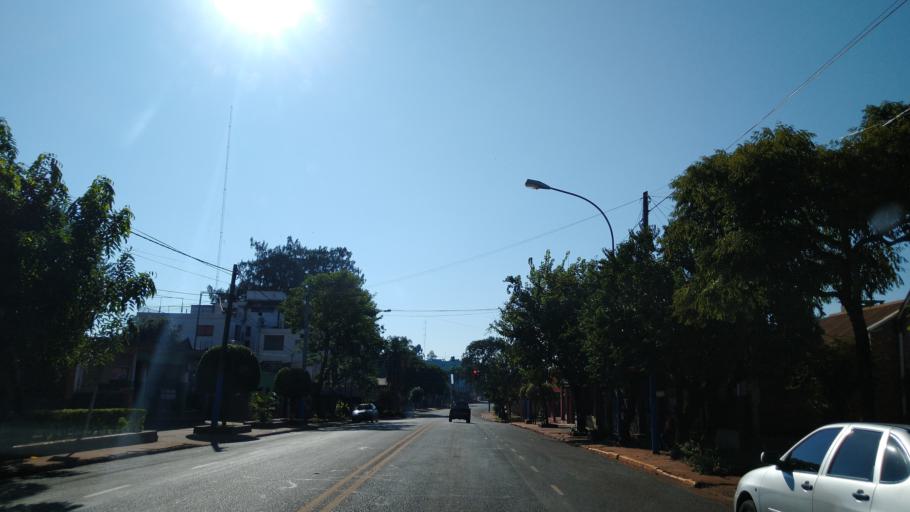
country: AR
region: Misiones
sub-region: Departamento de Montecarlo
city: Montecarlo
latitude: -26.5680
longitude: -54.7629
